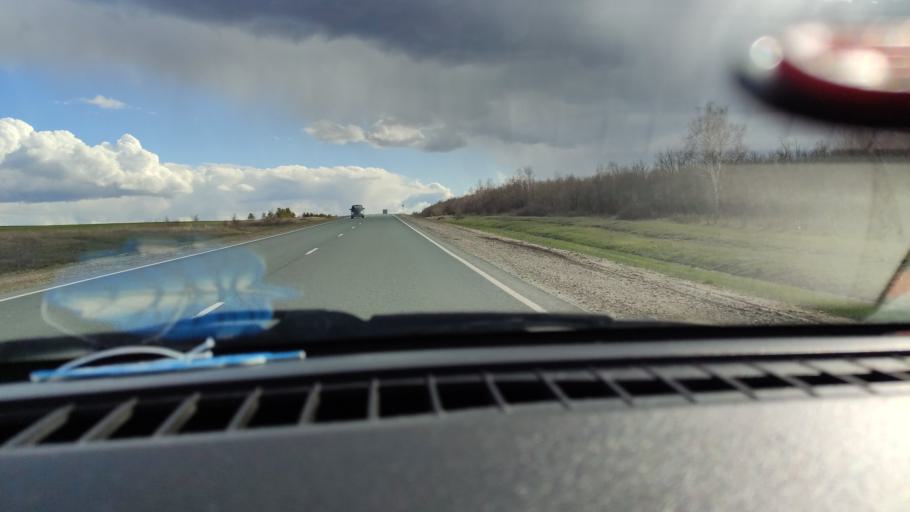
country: RU
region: Saratov
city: Alekseyevka
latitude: 52.2376
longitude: 47.9051
